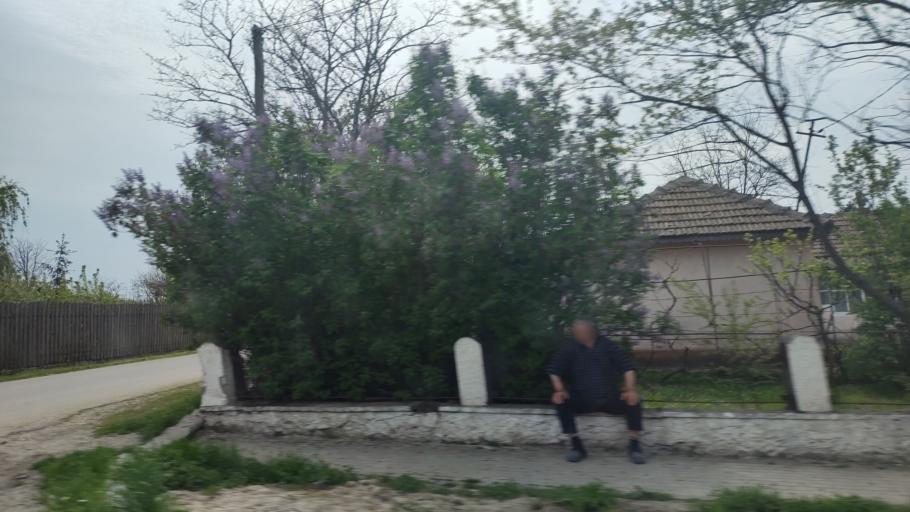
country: RO
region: Constanta
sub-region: Comuna Ciocarlia
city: Ciocarlia
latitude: 44.1050
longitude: 28.2925
